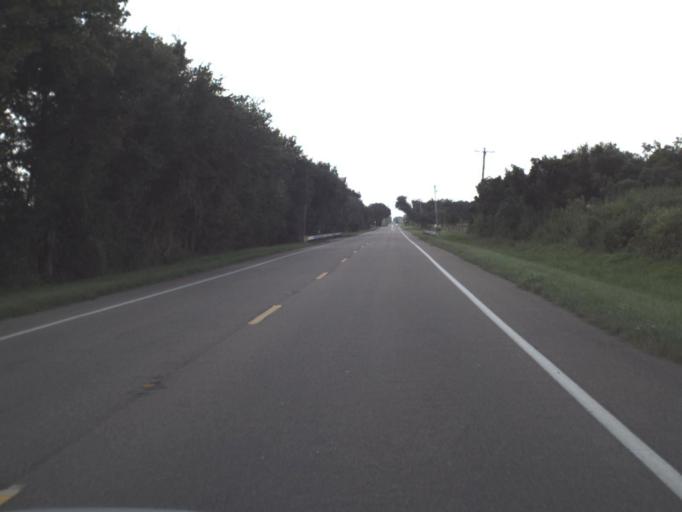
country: US
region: Florida
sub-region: Hardee County
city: Zolfo Springs
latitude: 27.4823
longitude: -81.9012
